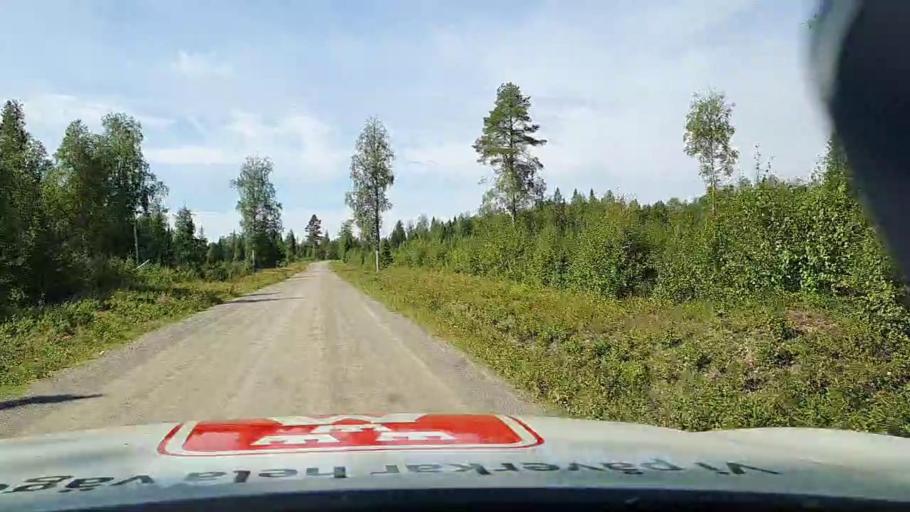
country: SE
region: Jaemtland
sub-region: Stroemsunds Kommun
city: Stroemsund
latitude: 63.7188
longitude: 15.2898
